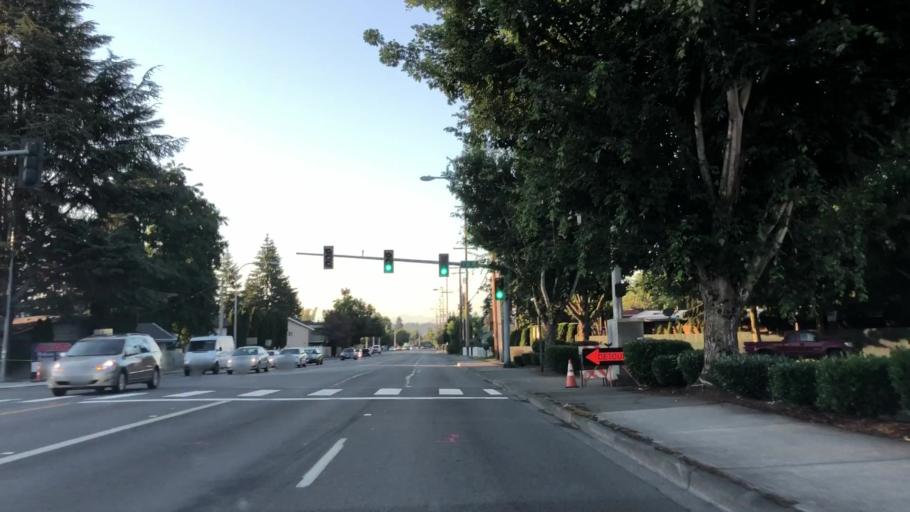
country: US
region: Washington
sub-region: King County
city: Auburn
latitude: 47.3199
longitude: -122.2200
